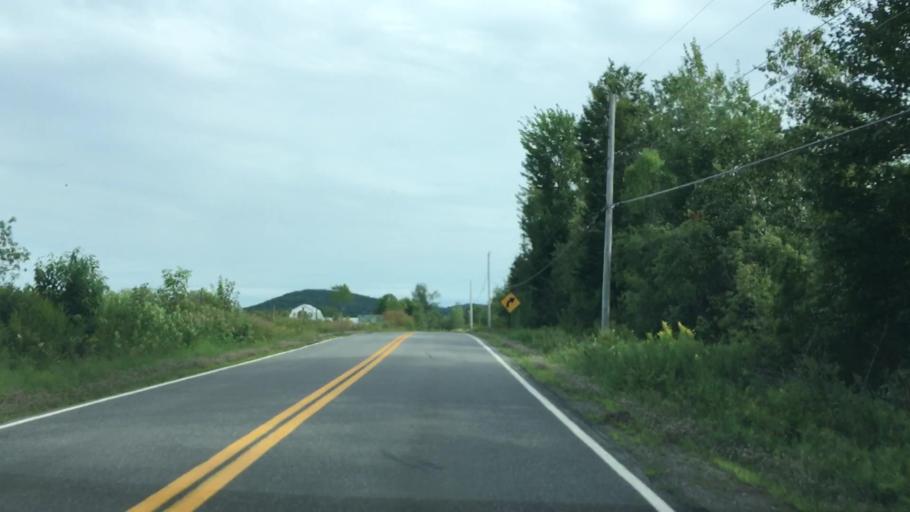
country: US
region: Maine
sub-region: Waldo County
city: Belfast
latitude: 44.3772
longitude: -69.0327
